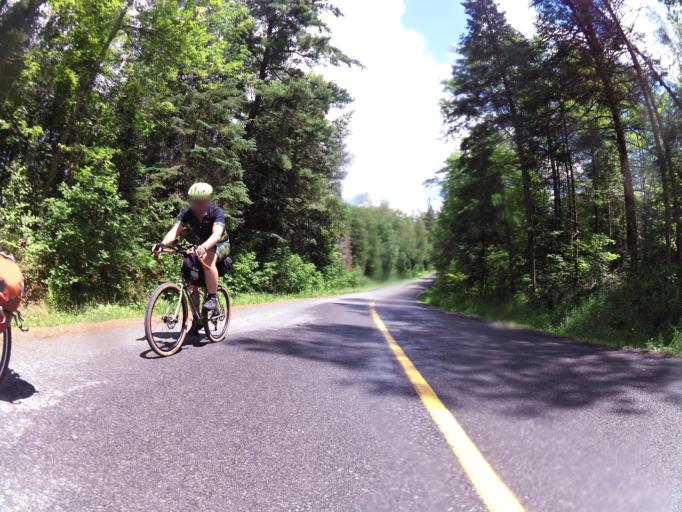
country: CA
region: Ontario
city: Renfrew
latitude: 45.0575
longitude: -76.6698
